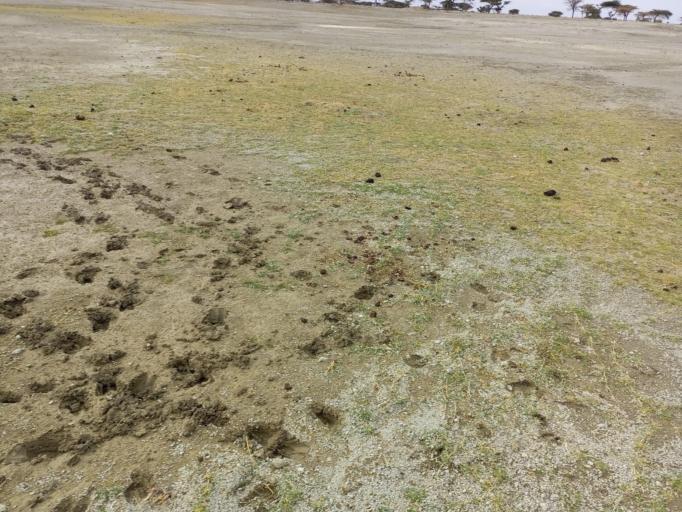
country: ET
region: Oromiya
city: Ziway
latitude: 7.6878
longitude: 38.6557
